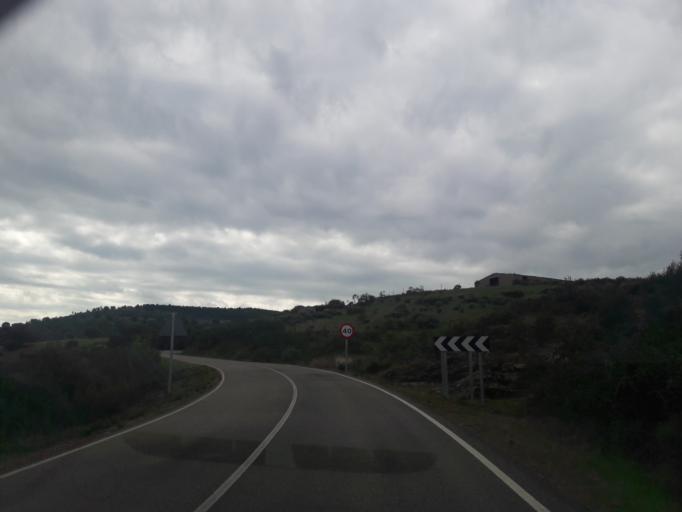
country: ES
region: Castille and Leon
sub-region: Provincia de Salamanca
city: Serradilla del Arroyo
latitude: 40.5248
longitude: -6.4037
